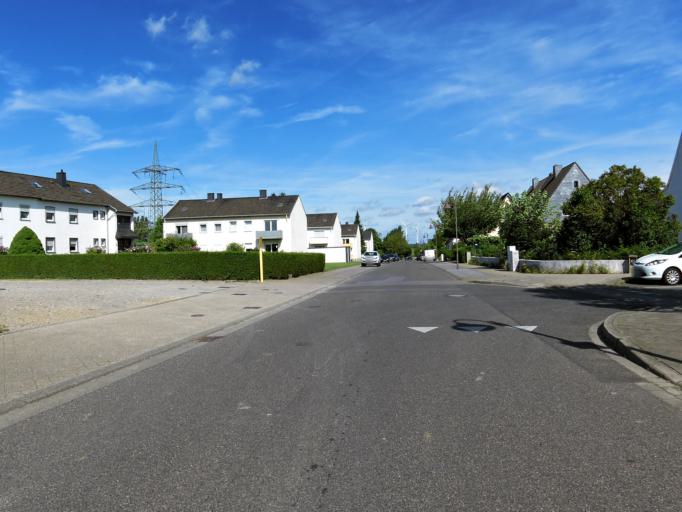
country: DE
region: North Rhine-Westphalia
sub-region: Regierungsbezirk Koln
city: Alsdorf
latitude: 50.8787
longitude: 6.1527
